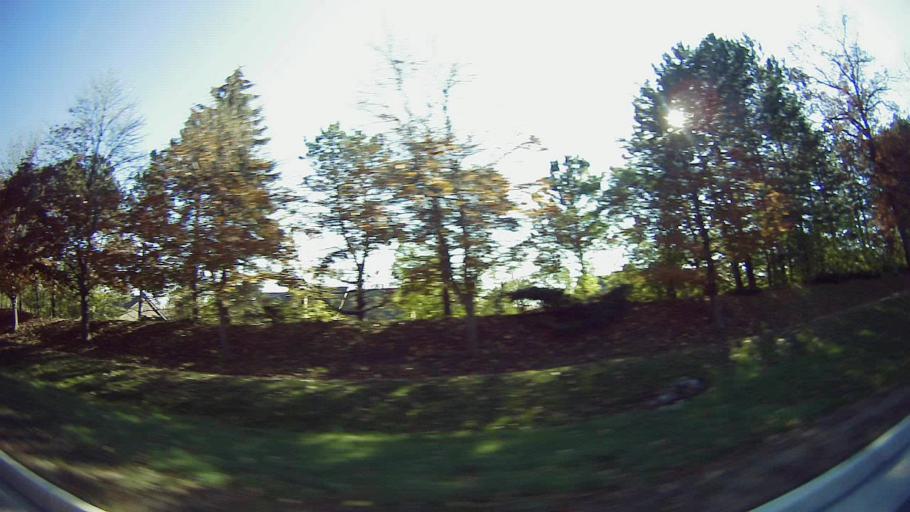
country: US
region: Michigan
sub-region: Oakland County
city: West Bloomfield Township
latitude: 42.5268
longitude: -83.4138
